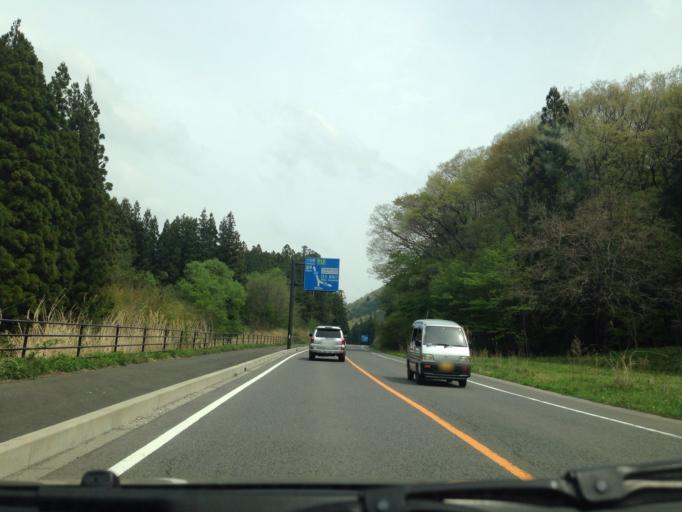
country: JP
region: Tochigi
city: Yaita
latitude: 36.9783
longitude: 139.7977
